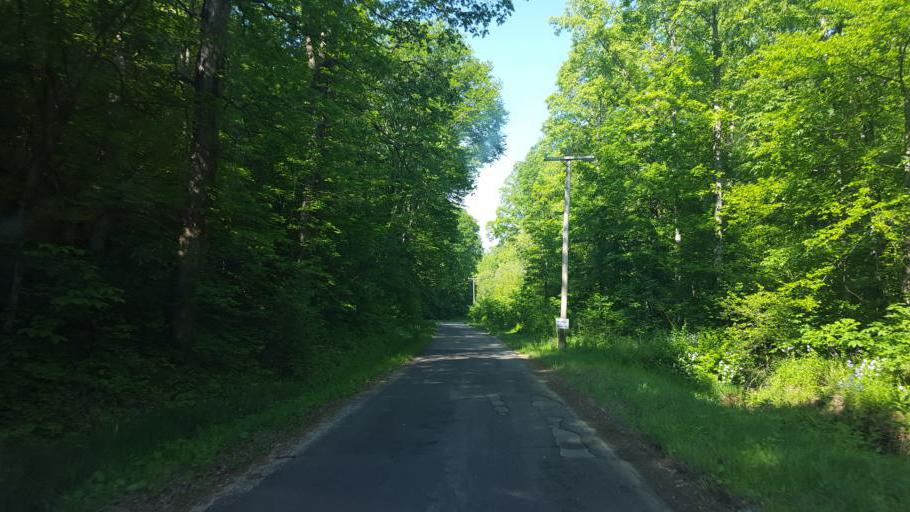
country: US
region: Ohio
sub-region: Jackson County
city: Oak Hill
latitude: 38.9899
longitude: -82.4986
